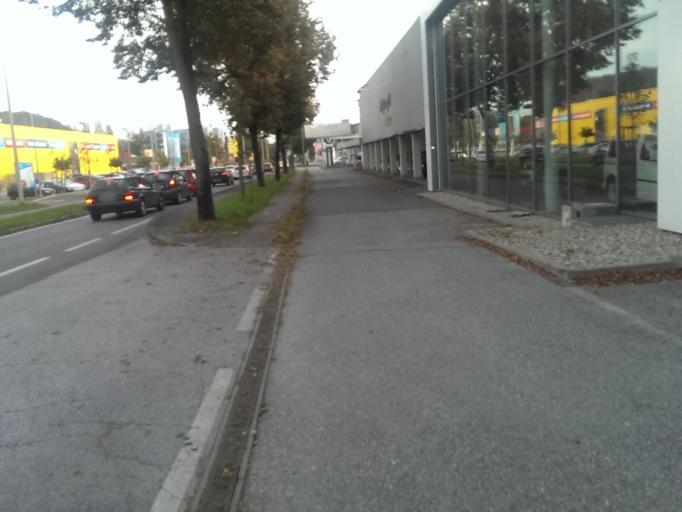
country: AT
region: Styria
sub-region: Graz Stadt
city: Goesting
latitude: 47.1027
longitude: 15.4149
